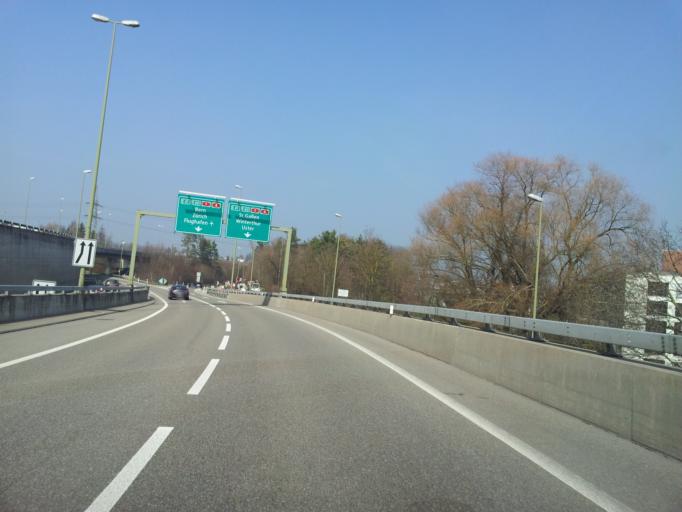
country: CH
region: Zurich
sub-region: Bezirk Buelach
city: Wallisellen / Wallisellen-Ost
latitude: 47.4040
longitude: 8.6000
